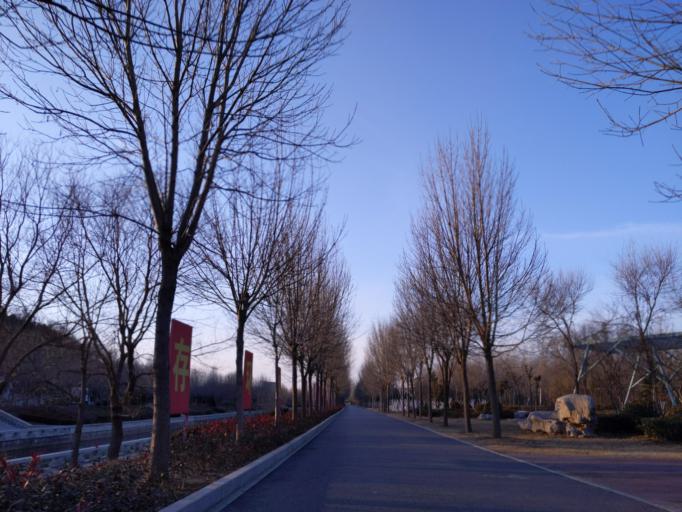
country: CN
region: Henan Sheng
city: Puyang
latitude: 35.7670
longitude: 115.0009
